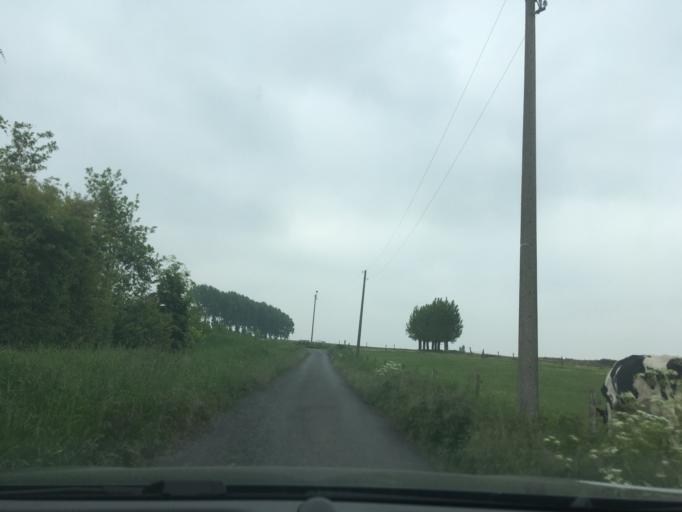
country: BE
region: Flanders
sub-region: Provincie West-Vlaanderen
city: Hooglede
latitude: 50.9937
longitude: 3.1113
